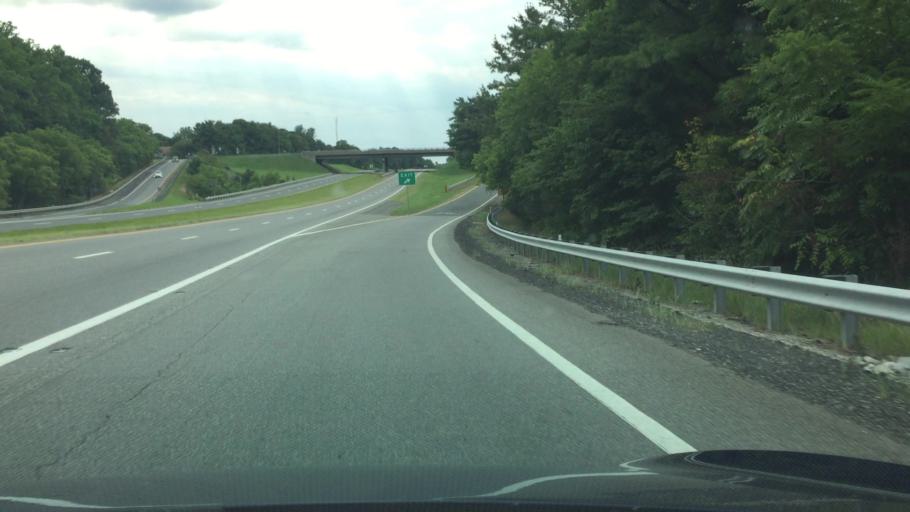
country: US
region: Virginia
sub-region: City of Bedford
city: Bedford
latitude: 37.3230
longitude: -79.5289
